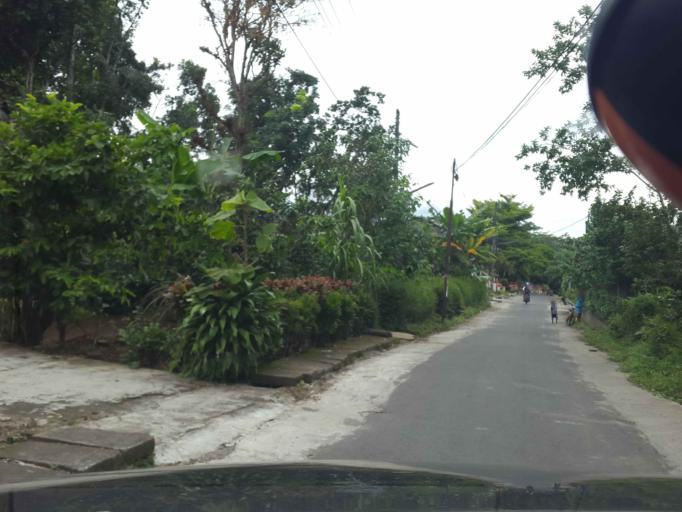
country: ID
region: Central Java
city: Salatiga
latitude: -7.3382
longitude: 110.4895
